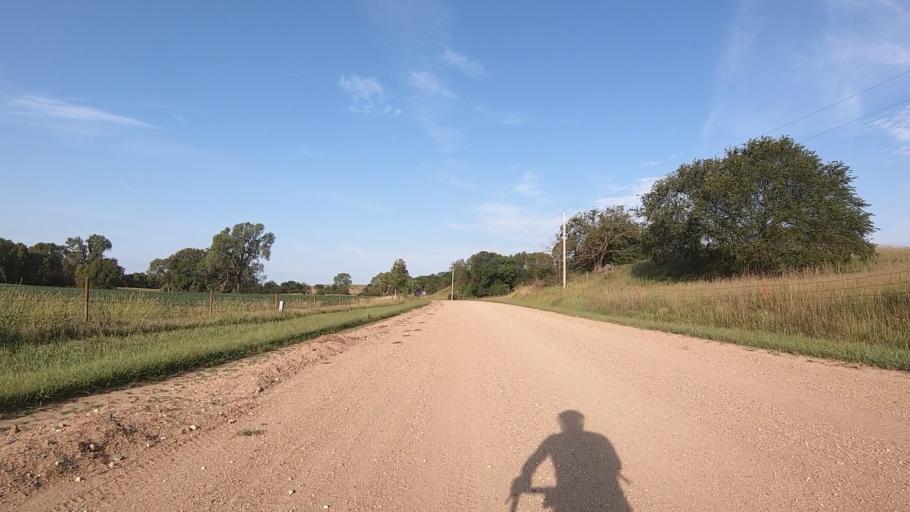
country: US
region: Kansas
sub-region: Marshall County
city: Blue Rapids
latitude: 39.6732
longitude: -96.8001
